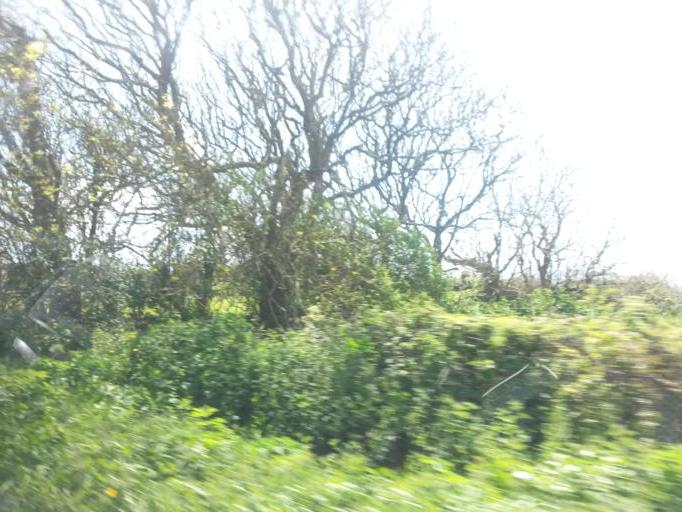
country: IE
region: Munster
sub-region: Waterford
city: Dunmore East
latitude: 52.1673
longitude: -6.8950
